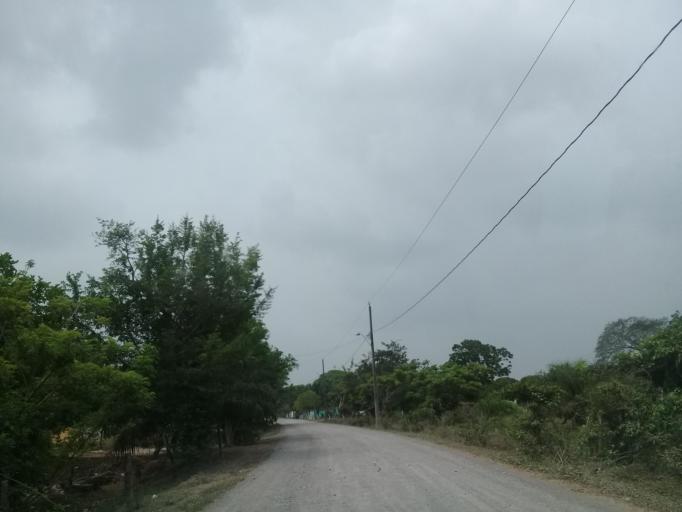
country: MX
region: Veracruz
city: El Tejar
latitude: 19.0590
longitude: -96.1982
